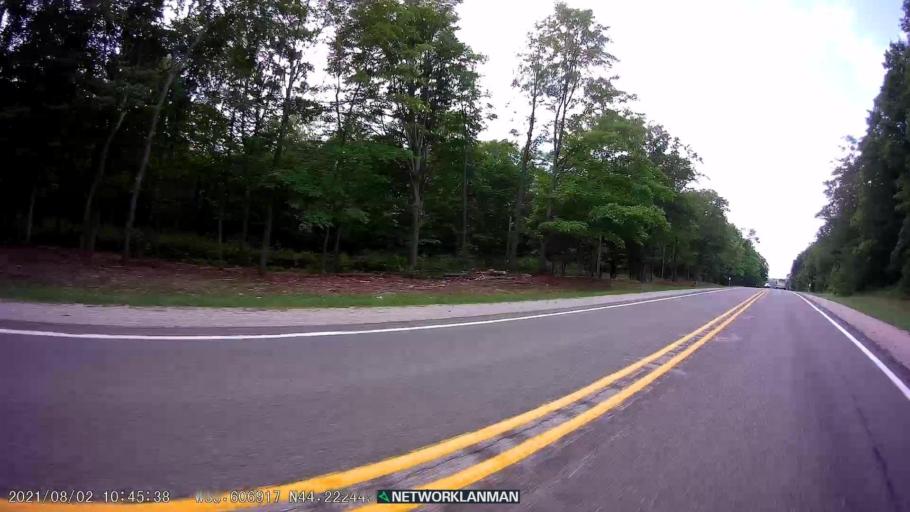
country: US
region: Michigan
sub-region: Wexford County
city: Cadillac
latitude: 44.2223
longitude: -85.6077
